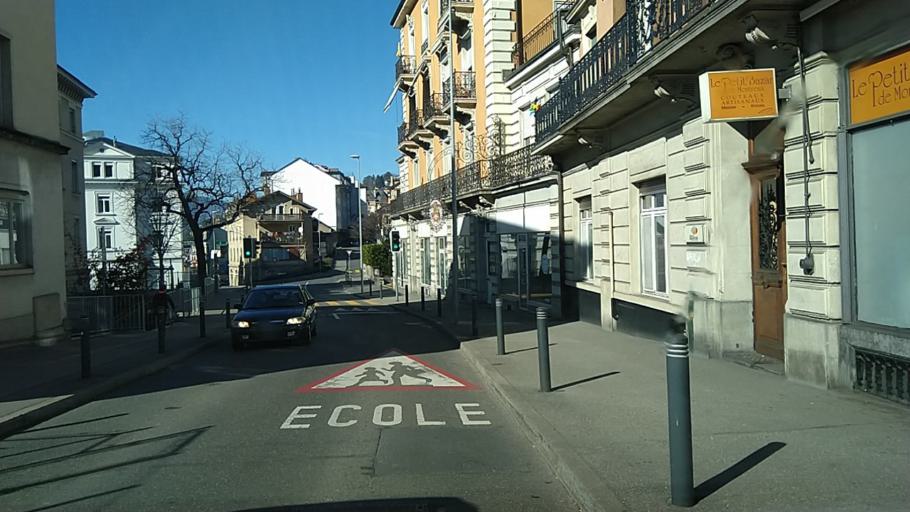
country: CH
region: Vaud
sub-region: Riviera-Pays-d'Enhaut District
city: Montreux
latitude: 46.4356
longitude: 6.9124
